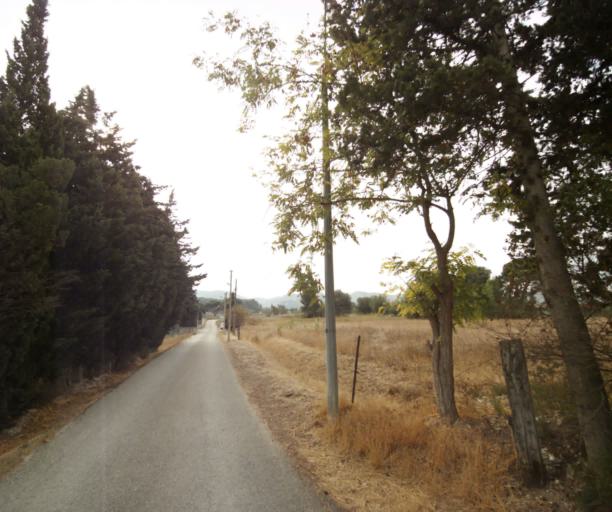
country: FR
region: Provence-Alpes-Cote d'Azur
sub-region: Departement des Bouches-du-Rhone
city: Gignac-la-Nerthe
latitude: 43.4043
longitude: 5.2669
